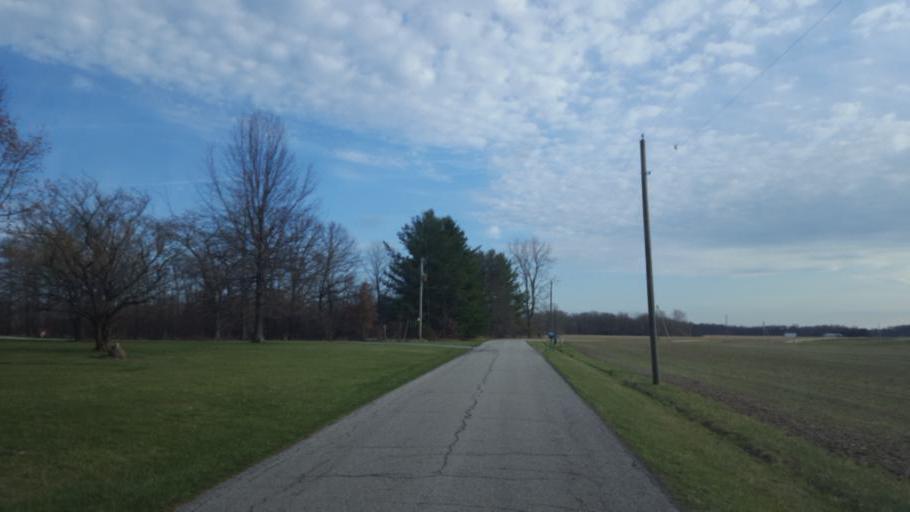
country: US
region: Ohio
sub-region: Crawford County
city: Bucyrus
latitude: 40.7278
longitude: -82.9356
